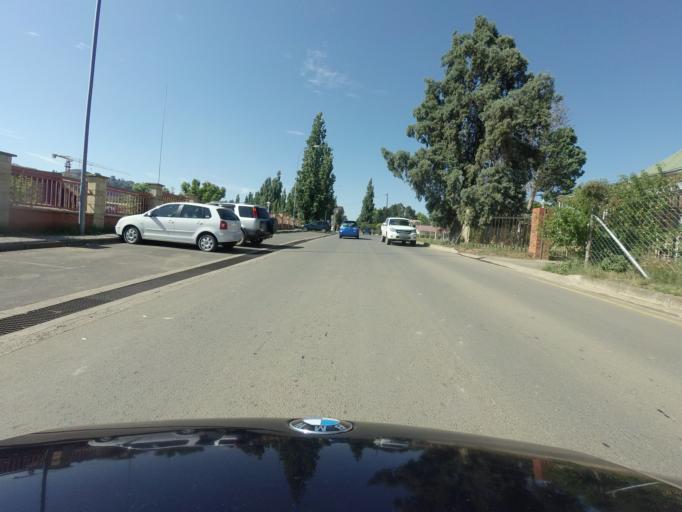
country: LS
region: Maseru
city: Maseru
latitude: -29.3109
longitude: 27.4871
